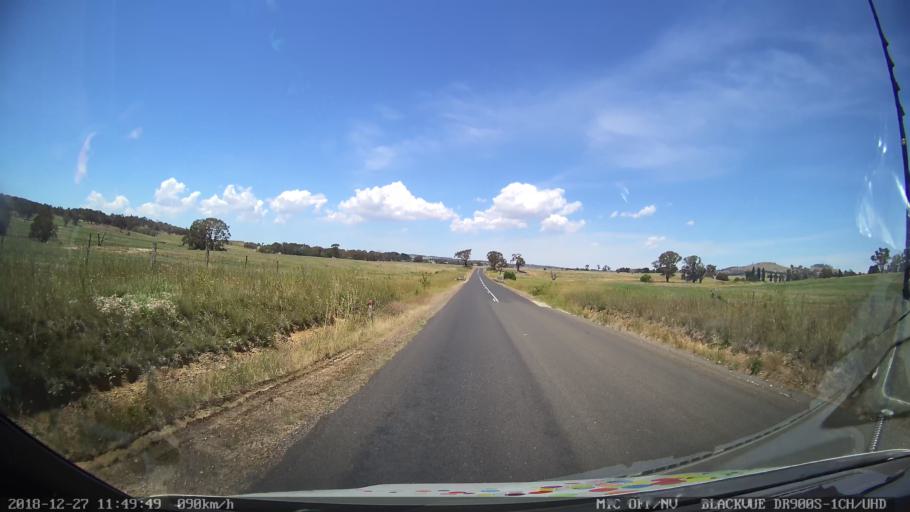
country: AU
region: New South Wales
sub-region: Bathurst Regional
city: Perthville
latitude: -33.6253
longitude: 149.4350
